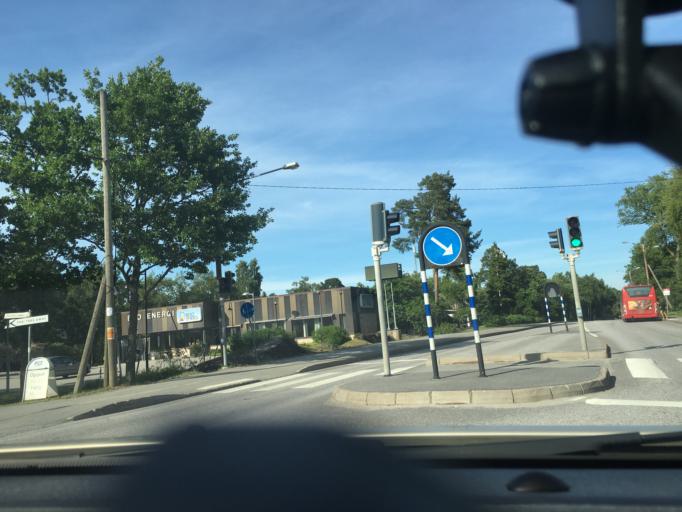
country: SE
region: Stockholm
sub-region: Nacka Kommun
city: Fisksatra
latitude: 59.3188
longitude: 18.2435
